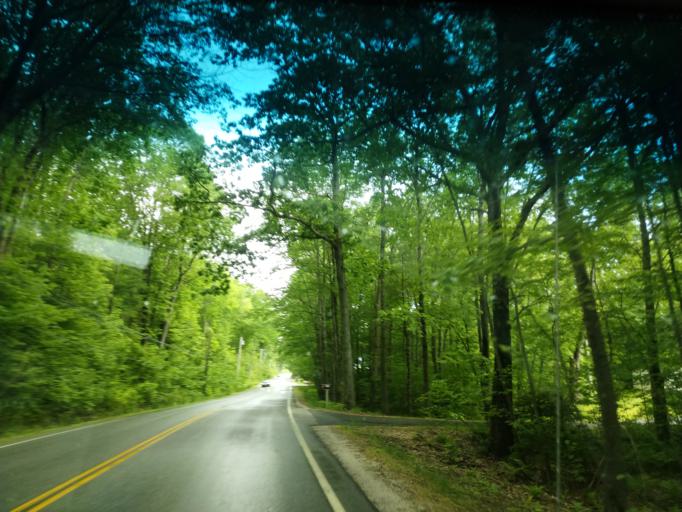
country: US
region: Maine
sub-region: Cumberland County
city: North Windham
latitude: 43.8042
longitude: -70.3706
